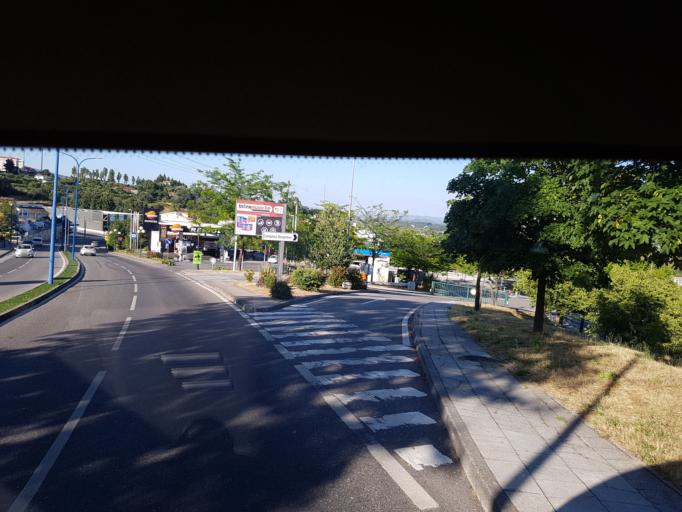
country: PT
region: Castelo Branco
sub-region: Covilha
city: Covilha
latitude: 40.2662
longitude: -7.5008
